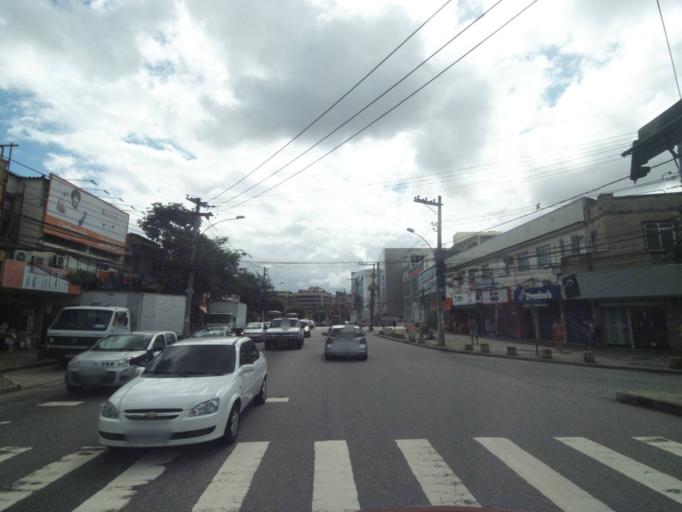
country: BR
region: Rio de Janeiro
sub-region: Sao Joao De Meriti
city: Sao Joao de Meriti
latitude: -22.9399
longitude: -43.3437
